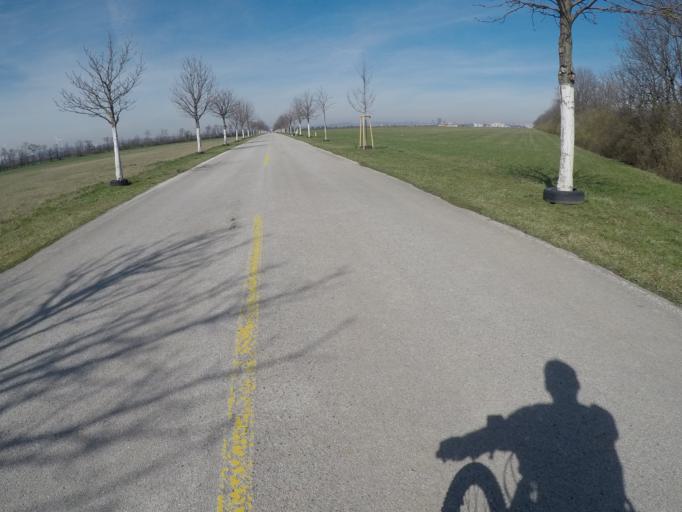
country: AT
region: Lower Austria
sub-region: Politischer Bezirk Modling
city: Vosendorf
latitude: 48.1023
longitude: 16.3413
